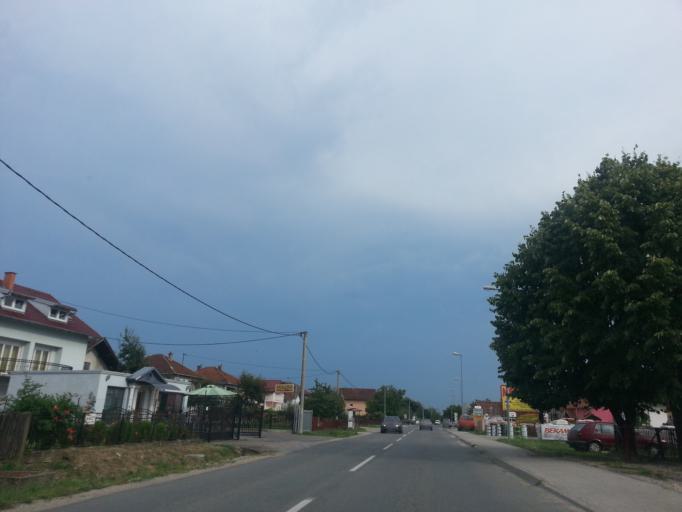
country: BA
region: Brcko
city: Brcko
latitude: 44.8507
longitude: 18.8160
